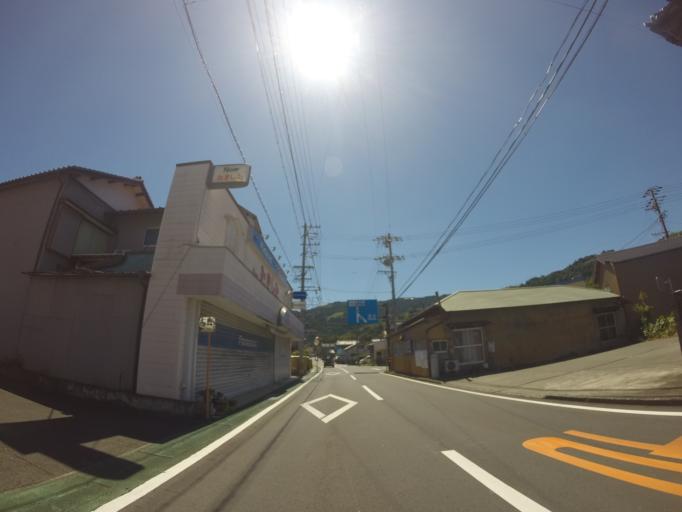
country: JP
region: Shizuoka
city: Fujieda
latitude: 34.9035
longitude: 138.1990
